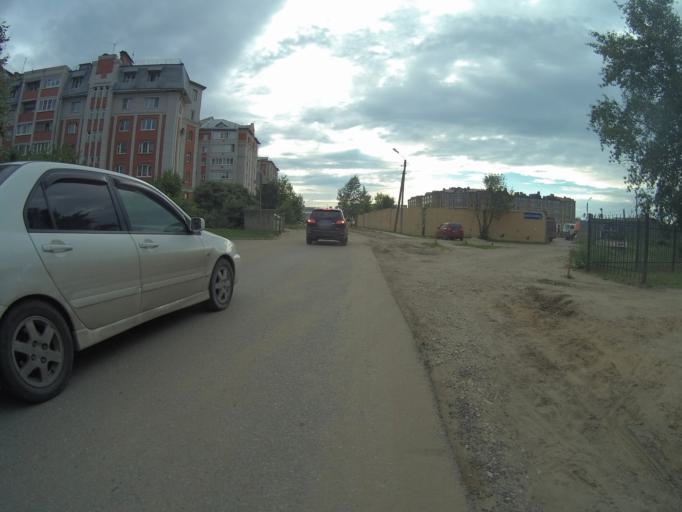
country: RU
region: Vladimir
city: Kommunar
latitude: 56.1081
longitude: 40.4421
